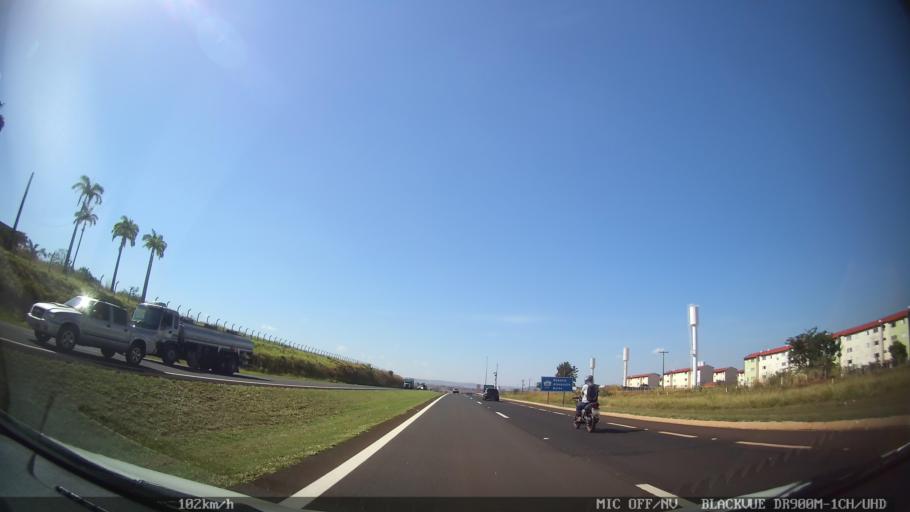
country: BR
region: Sao Paulo
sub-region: Ribeirao Preto
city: Ribeirao Preto
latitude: -21.1139
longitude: -47.8223
